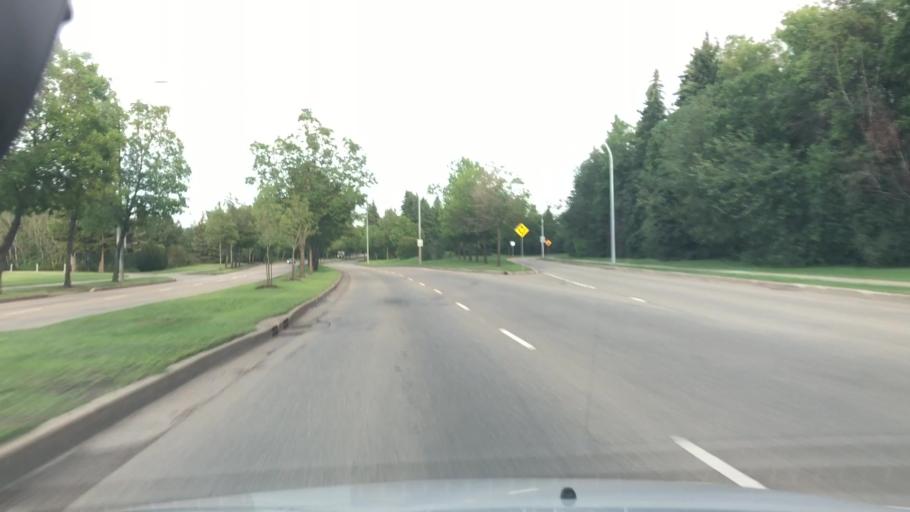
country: CA
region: Alberta
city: St. Albert
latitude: 53.6405
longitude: -113.5998
